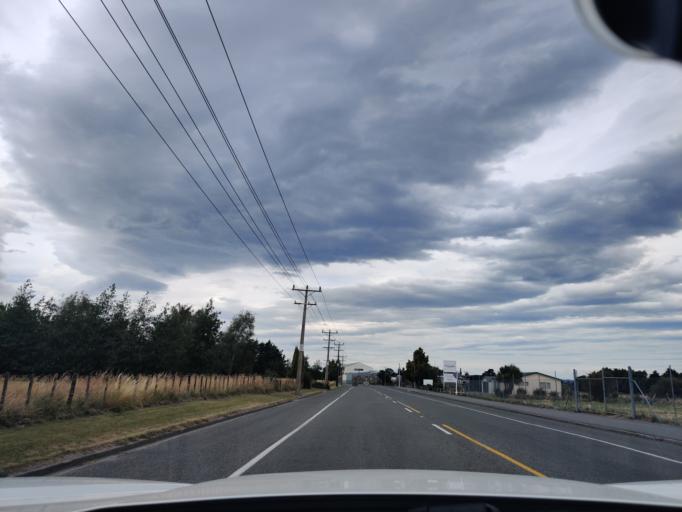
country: NZ
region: Wellington
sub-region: Masterton District
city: Masterton
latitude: -40.9515
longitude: 175.6287
